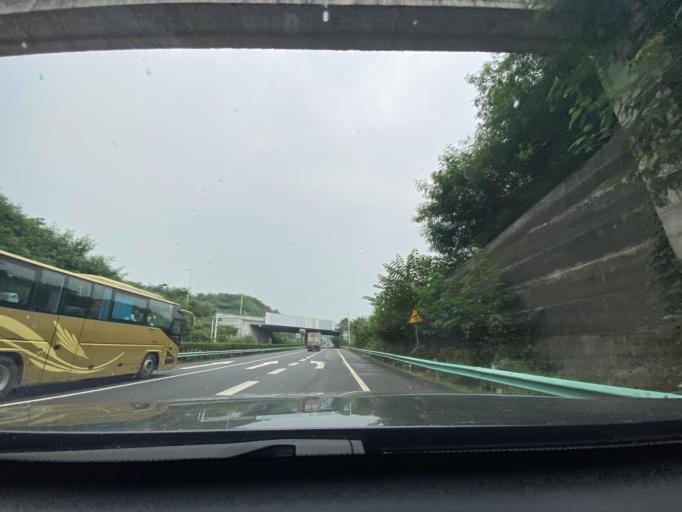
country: CN
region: Sichuan
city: Longquan
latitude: 30.2987
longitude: 104.1222
